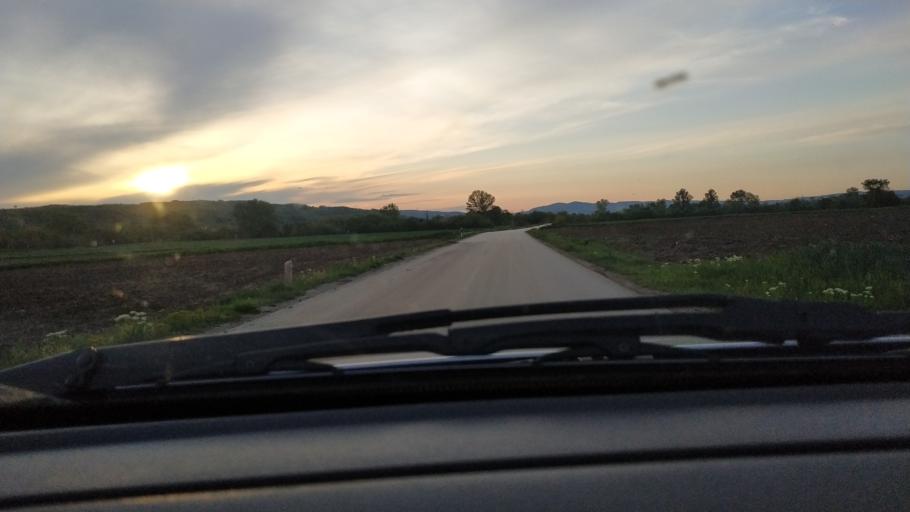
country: RS
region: Central Serbia
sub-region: Nisavski Okrug
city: Aleksinac
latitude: 43.5468
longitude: 21.6231
